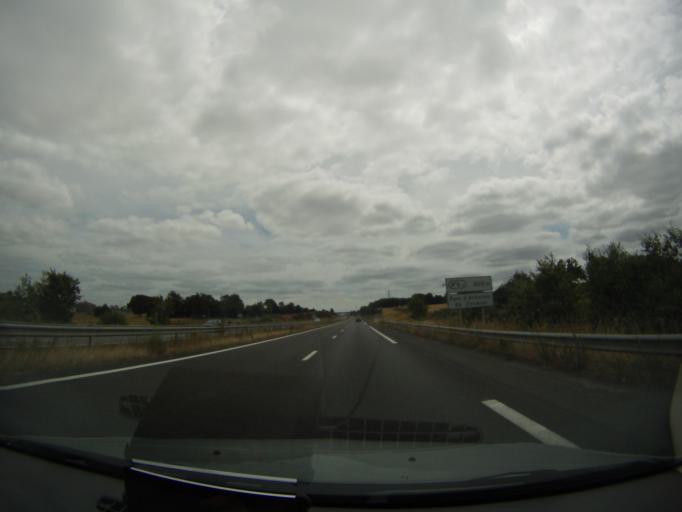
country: FR
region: Pays de la Loire
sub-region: Departement de Maine-et-Loire
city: La Seguiniere
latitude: 47.0538
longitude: -0.9203
